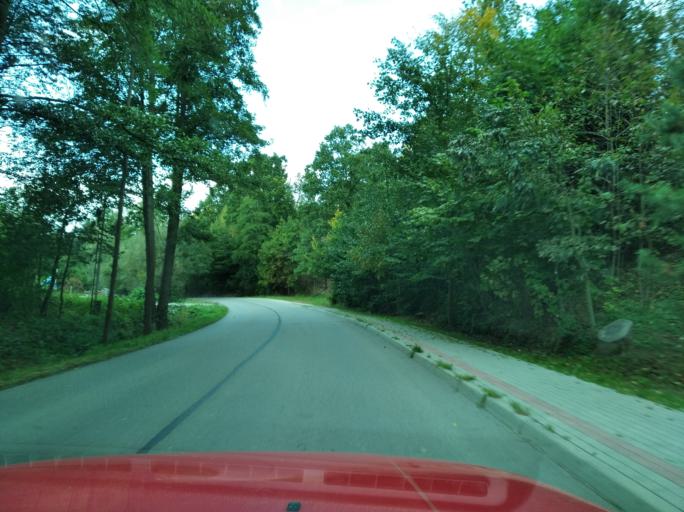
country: PL
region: Subcarpathian Voivodeship
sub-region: Powiat rzeszowski
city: Tyczyn
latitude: 49.9332
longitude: 22.0202
